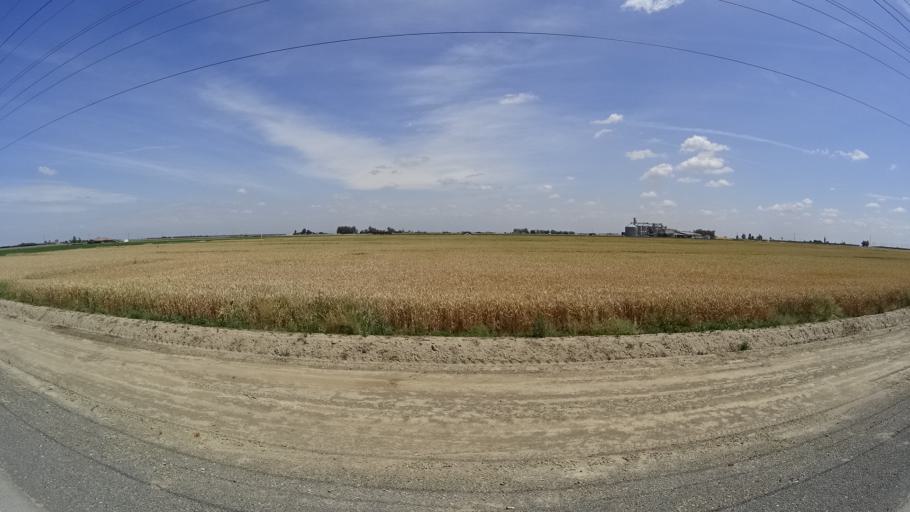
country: US
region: California
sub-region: Kings County
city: Home Garden
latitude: 36.2211
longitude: -119.6549
